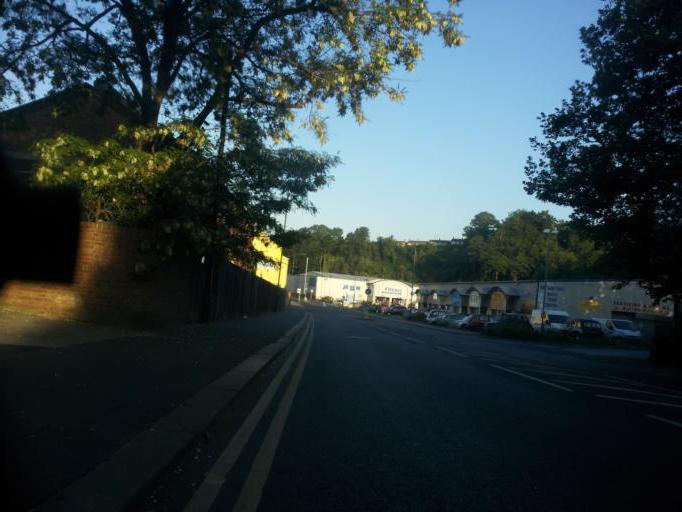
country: GB
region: England
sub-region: Greater London
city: Erith
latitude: 51.4830
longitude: 0.1665
